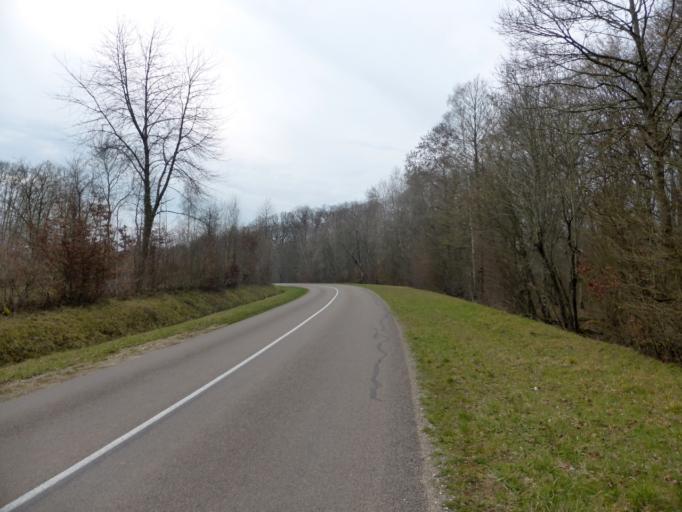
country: FR
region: Champagne-Ardenne
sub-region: Departement de l'Aube
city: Lusigny-sur-Barse
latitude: 48.2760
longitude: 4.3027
